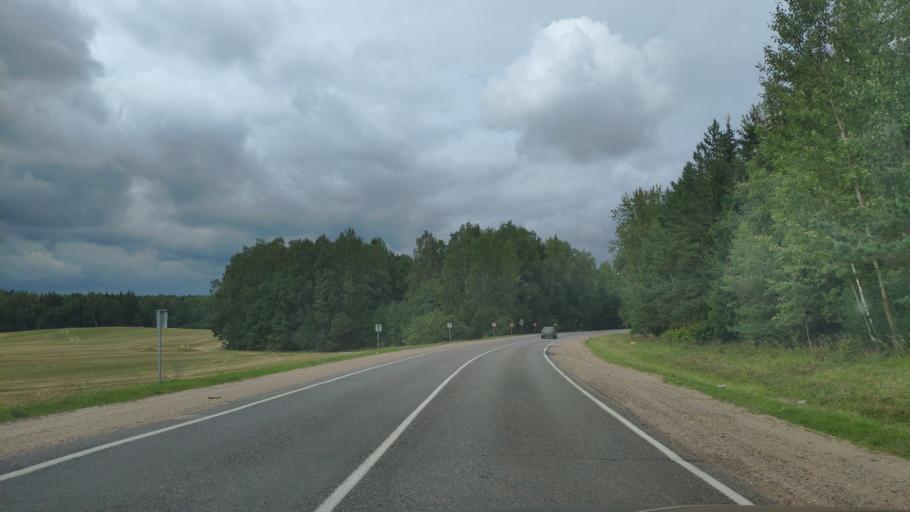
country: BY
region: Minsk
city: Zaslawye
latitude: 53.9645
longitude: 27.2446
